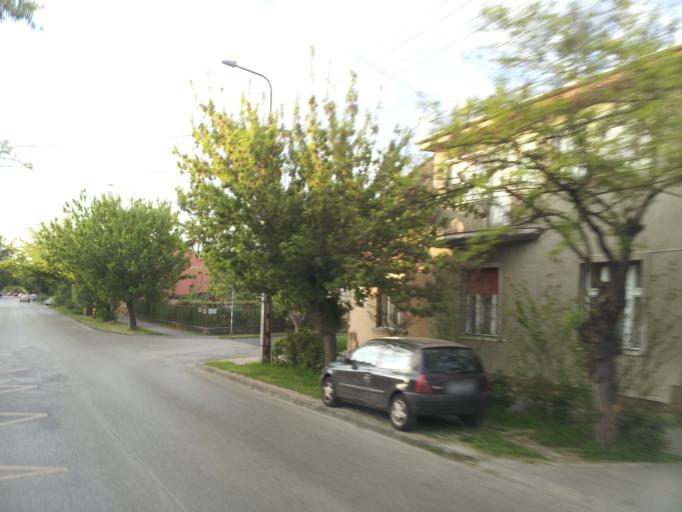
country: HU
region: Budapest
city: Budapest XV. keruelet
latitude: 47.5470
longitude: 19.1094
